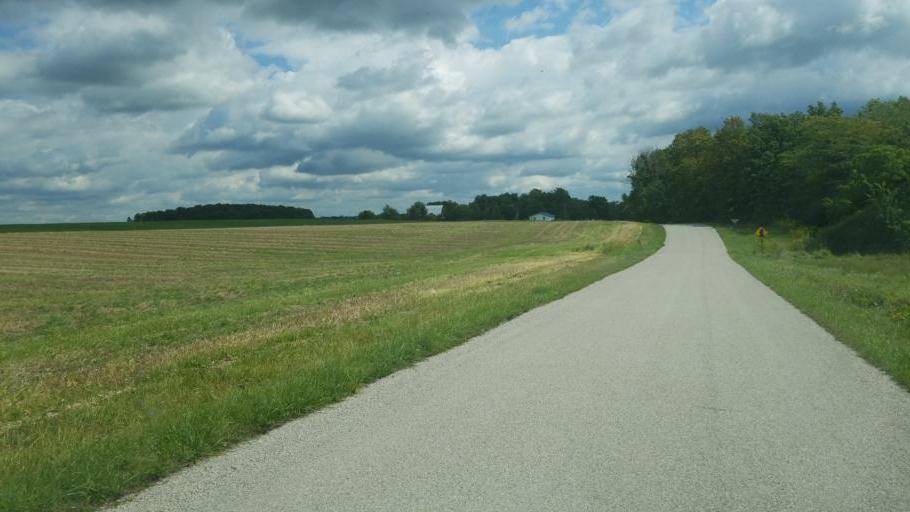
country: US
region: Ohio
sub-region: Huron County
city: Willard
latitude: 41.1166
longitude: -82.8333
